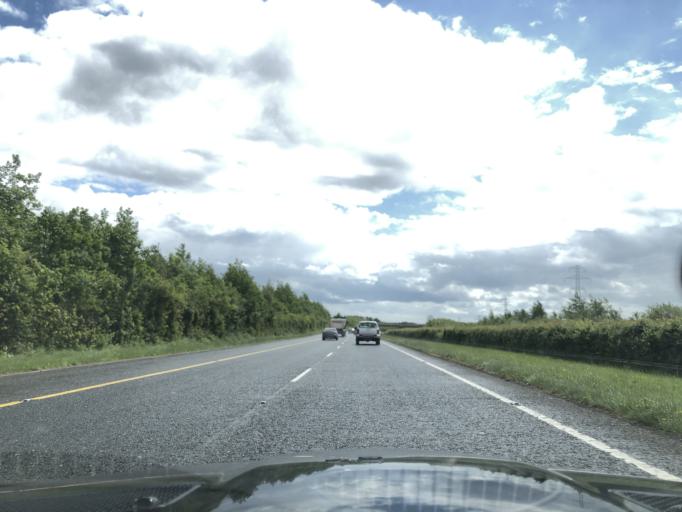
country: IE
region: Leinster
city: Lusk
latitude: 53.5123
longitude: -6.2055
